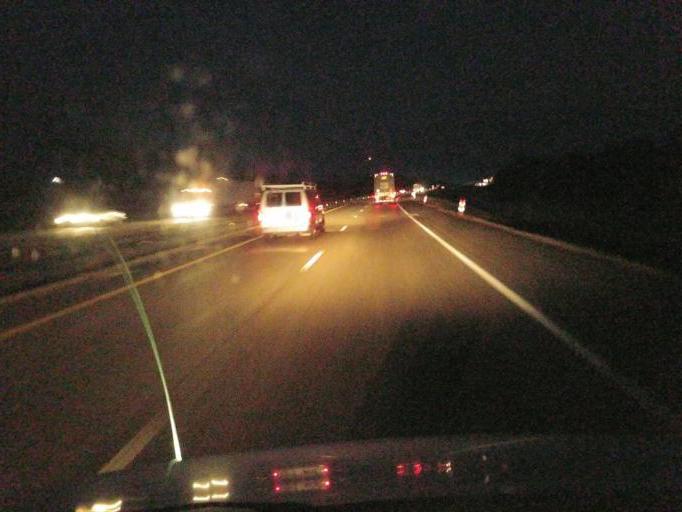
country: US
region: Missouri
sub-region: Franklin County
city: Saint Clair
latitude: 38.3242
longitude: -91.0270
